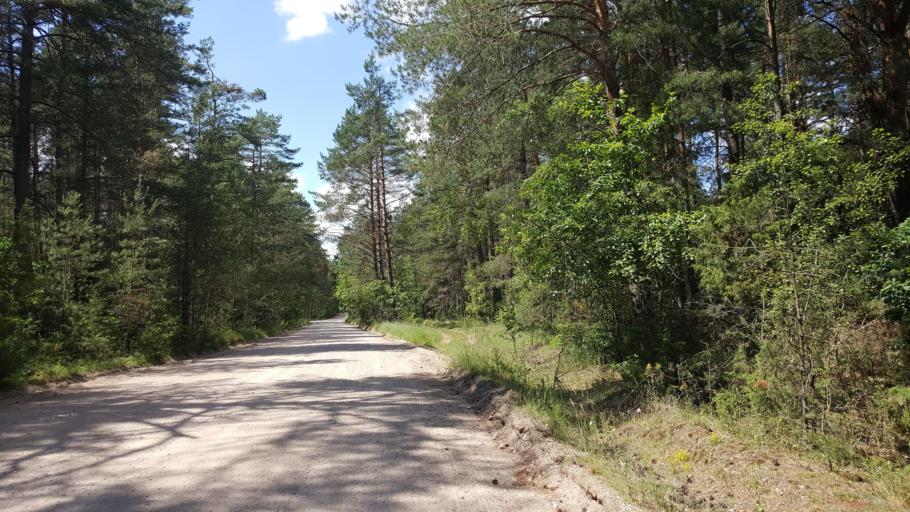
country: BY
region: Brest
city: Kamyanyuki
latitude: 52.5620
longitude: 23.7890
